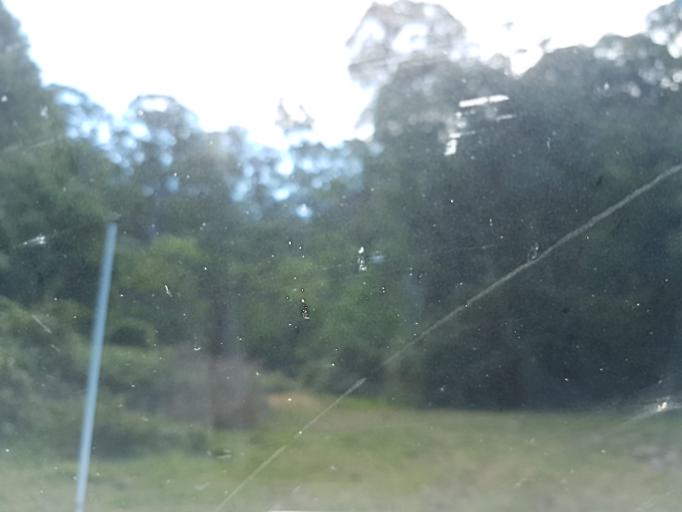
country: AU
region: Victoria
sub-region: Alpine
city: Mount Beauty
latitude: -36.9117
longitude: 147.0483
